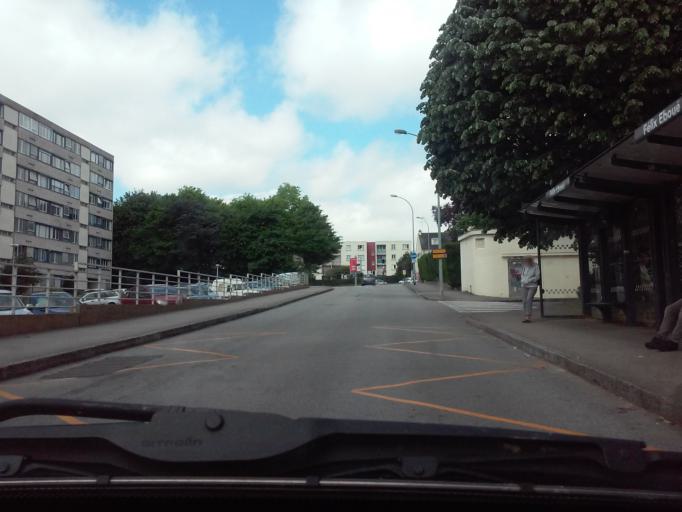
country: FR
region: Brittany
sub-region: Departement d'Ille-et-Vilaine
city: Rennes
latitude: 48.0857
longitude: -1.6939
